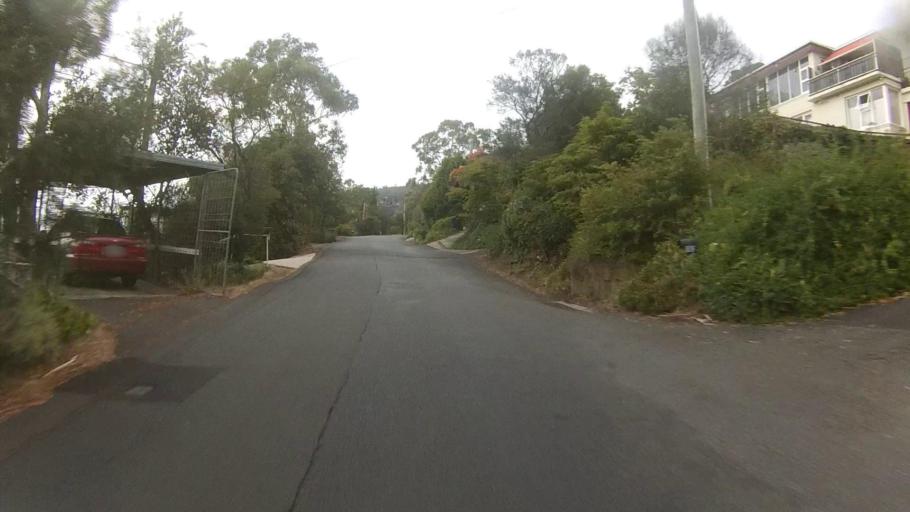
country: AU
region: Tasmania
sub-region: Hobart
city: Dynnyrne
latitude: -42.9098
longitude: 147.3269
